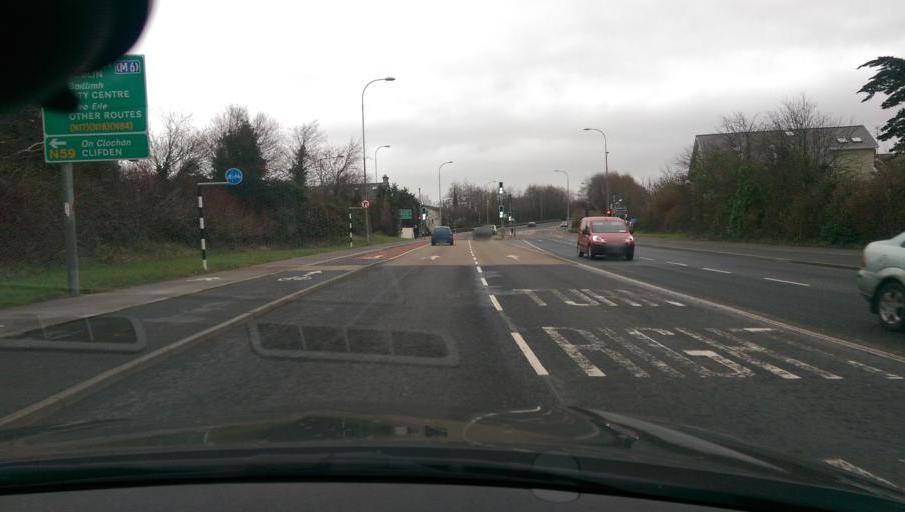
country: IE
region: Connaught
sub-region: County Galway
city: Gaillimh
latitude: 53.2817
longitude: -9.0669
